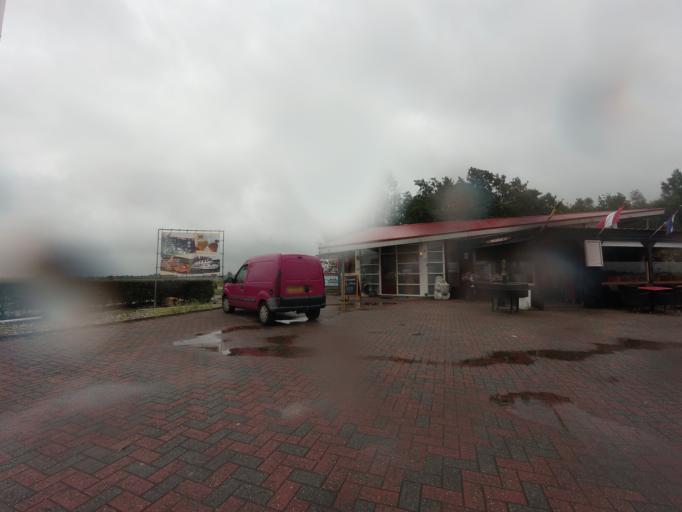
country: NL
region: Friesland
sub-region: Gemeente Tytsjerksteradiel
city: Garyp
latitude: 53.1349
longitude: 5.9534
